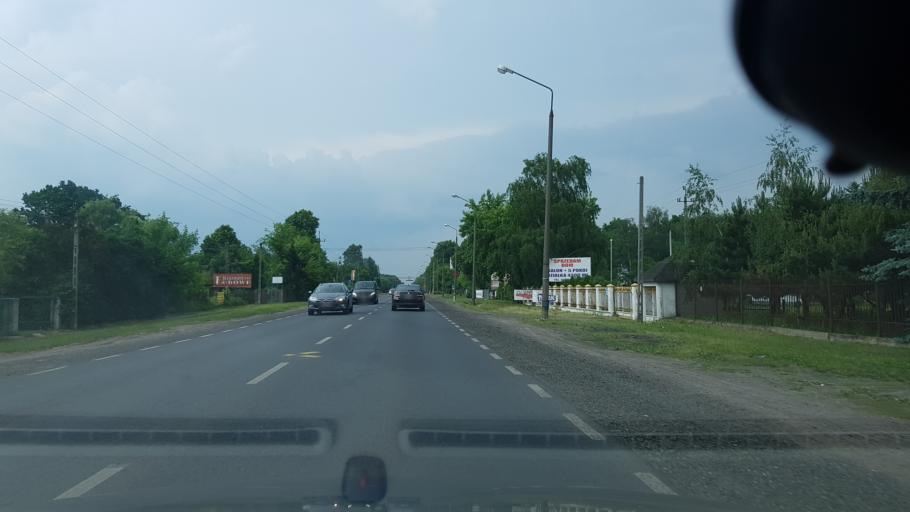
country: PL
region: Masovian Voivodeship
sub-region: Powiat legionowski
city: Michalow-Reginow
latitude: 52.4250
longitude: 20.9762
